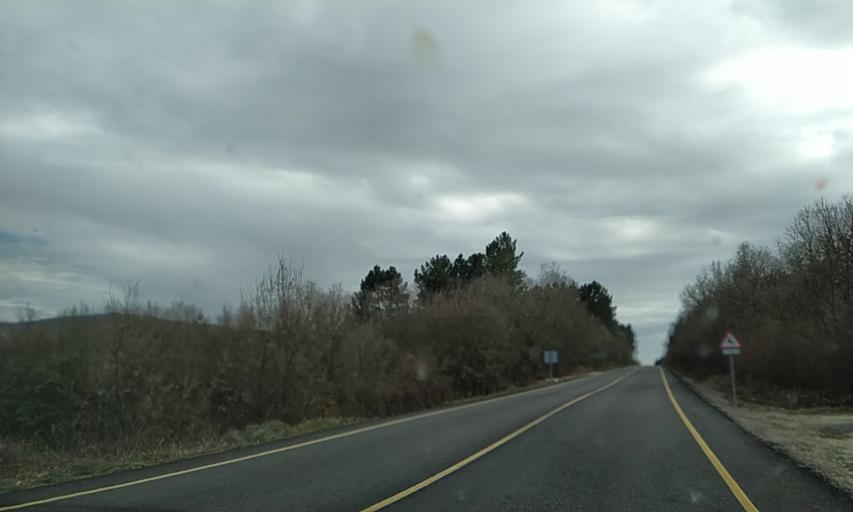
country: ES
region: Castille and Leon
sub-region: Provincia de Salamanca
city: Penaparda
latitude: 40.3122
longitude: -6.6479
